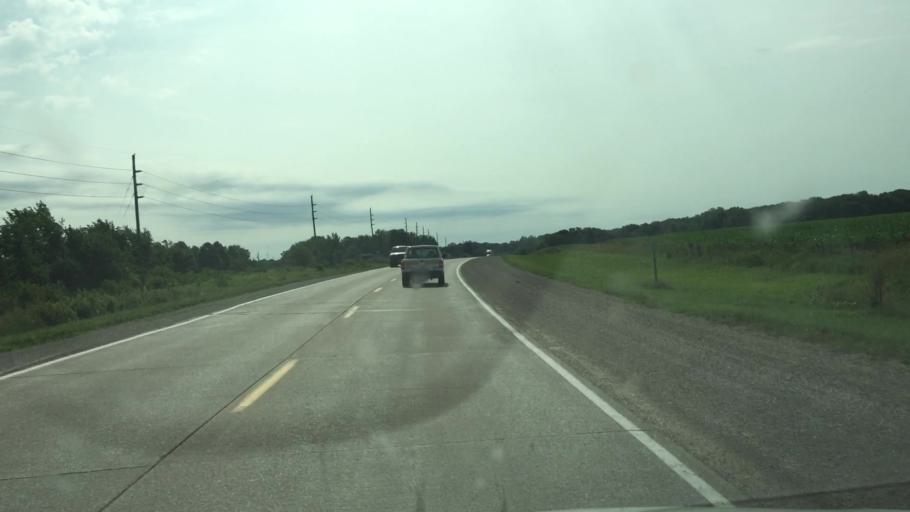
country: US
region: Illinois
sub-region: Hancock County
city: Nauvoo
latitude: 40.6318
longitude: -91.4995
